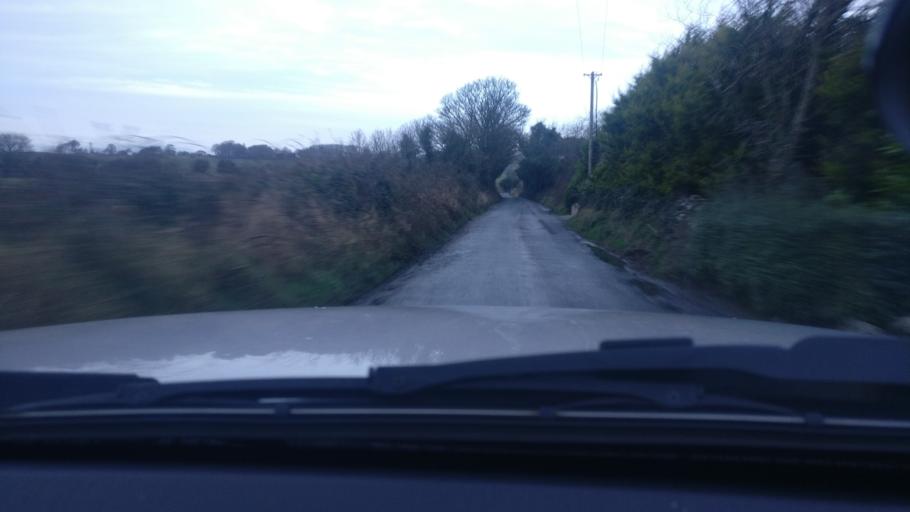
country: IE
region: Connaught
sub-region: County Galway
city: Loughrea
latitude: 53.1696
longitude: -8.5081
